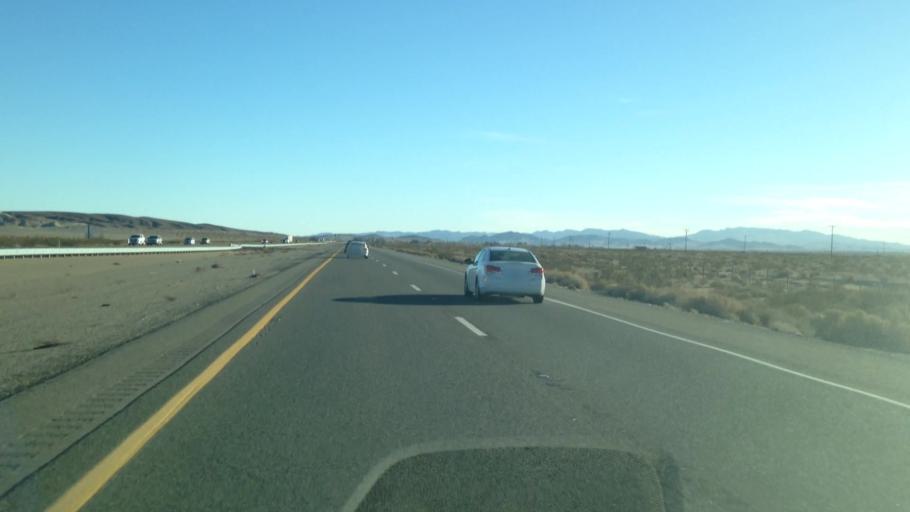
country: US
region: California
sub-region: San Bernardino County
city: Barstow
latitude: 34.9235
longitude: -116.7446
